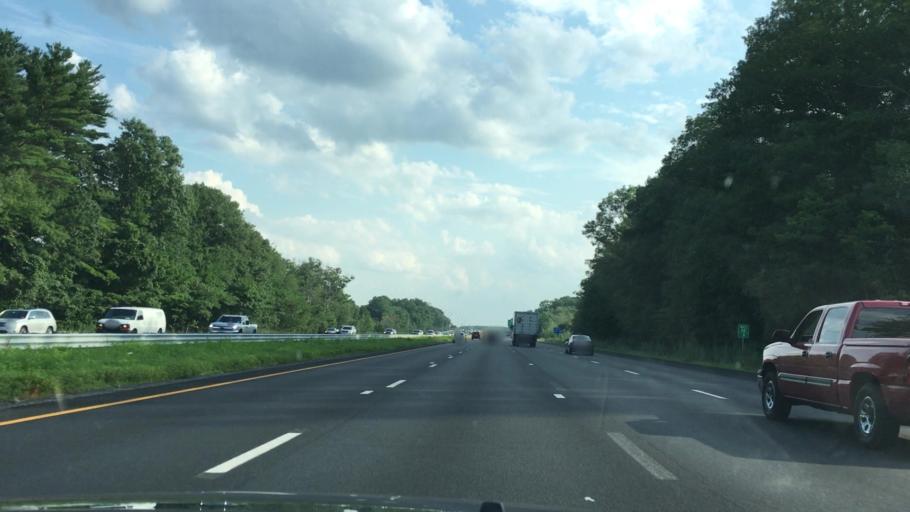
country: US
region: Massachusetts
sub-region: Essex County
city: Amesbury
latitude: 42.8543
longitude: -70.8979
